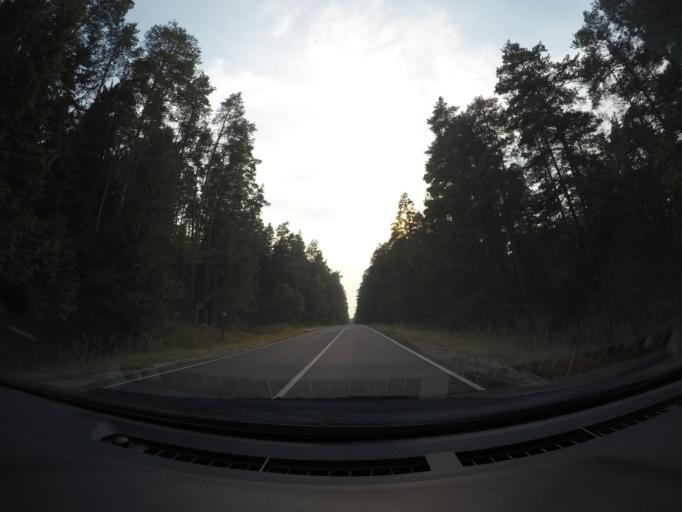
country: RU
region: Moskovskaya
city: Imeni Tsyurupy
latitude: 55.5030
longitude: 38.7114
